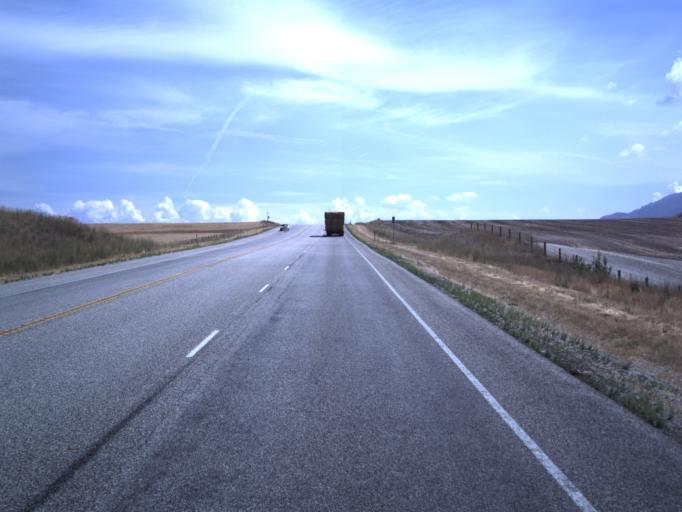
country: US
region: Utah
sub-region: Cache County
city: Mendon
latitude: 41.7829
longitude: -112.0251
